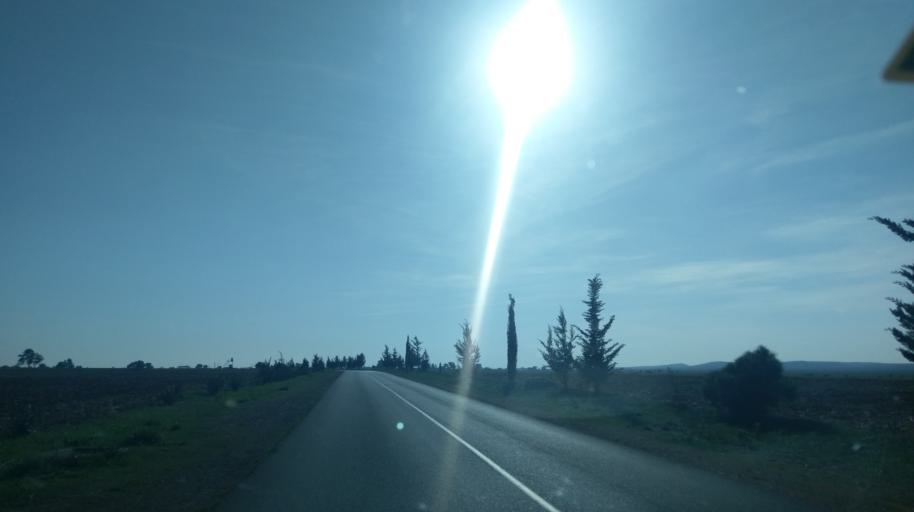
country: CY
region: Larnaka
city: Pergamos
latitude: 35.0733
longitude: 33.7178
